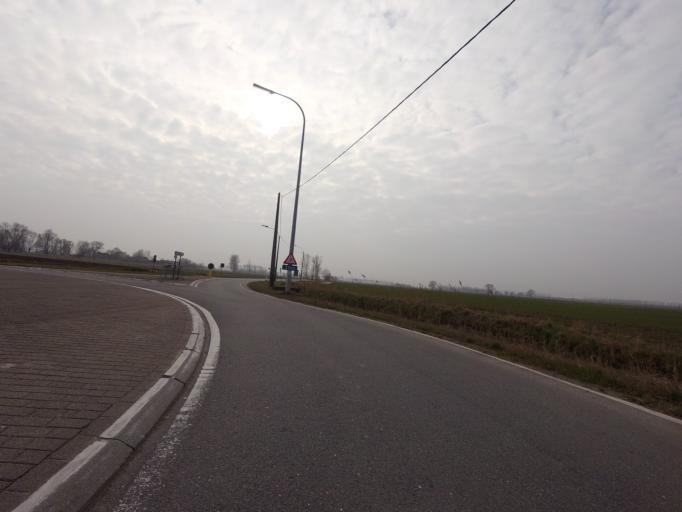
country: BE
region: Flanders
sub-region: Provincie Oost-Vlaanderen
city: Beveren
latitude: 51.3221
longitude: 4.2494
